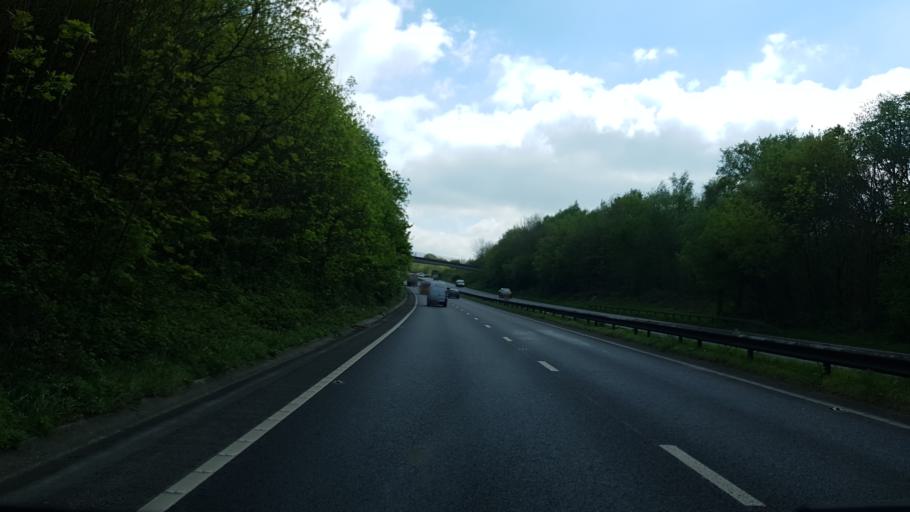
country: GB
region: England
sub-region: Kent
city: Pembury
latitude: 51.1407
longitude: 0.3164
